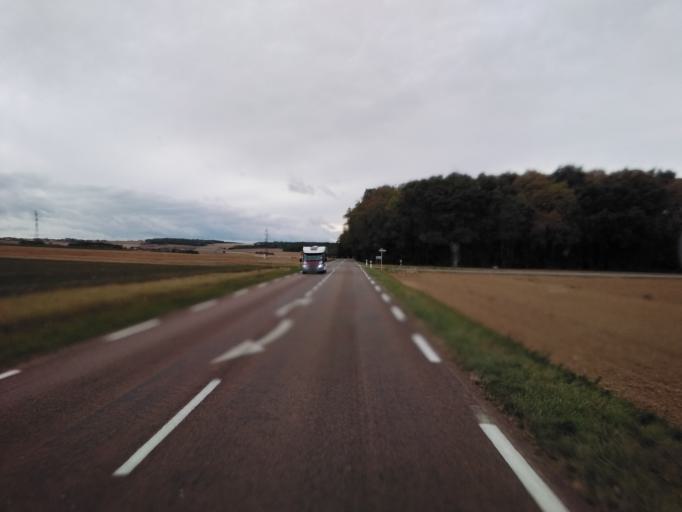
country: FR
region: Champagne-Ardenne
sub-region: Departement de l'Aube
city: Vendeuvre-sur-Barse
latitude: 48.2030
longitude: 4.4412
